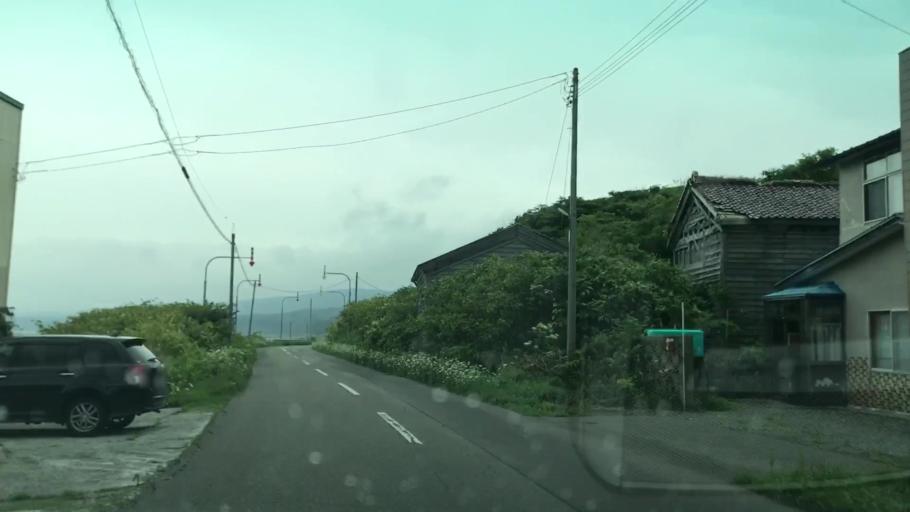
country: JP
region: Hokkaido
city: Iwanai
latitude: 42.7901
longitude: 140.2374
